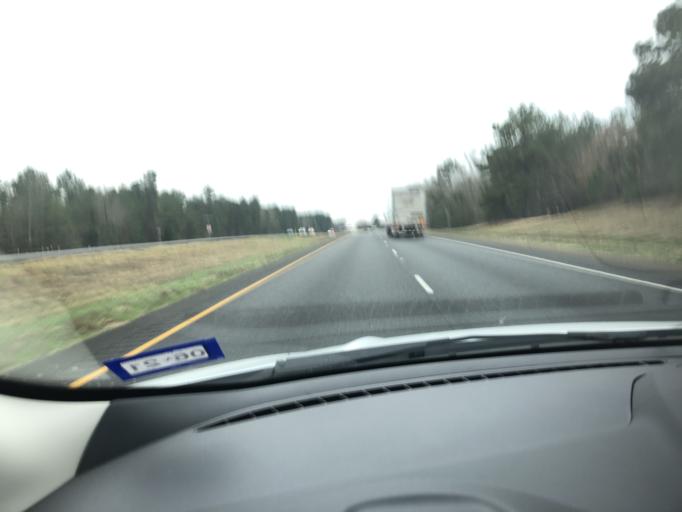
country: US
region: Texas
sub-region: Nacogdoches County
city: Nacogdoches
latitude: 31.5125
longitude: -94.7002
